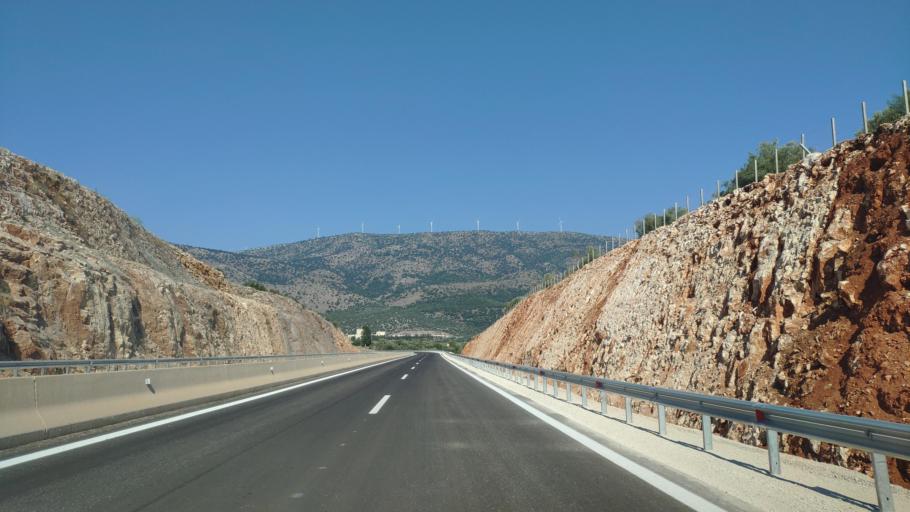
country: GR
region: West Greece
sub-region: Nomos Aitolias kai Akarnanias
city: Stanos
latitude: 38.7721
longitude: 21.1734
